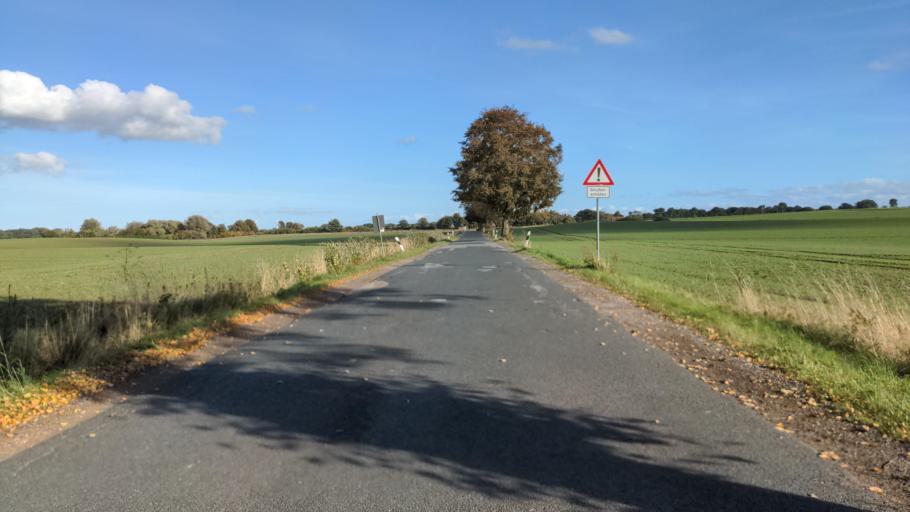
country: DE
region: Schleswig-Holstein
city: Beschendorf
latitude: 54.1999
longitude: 10.8773
